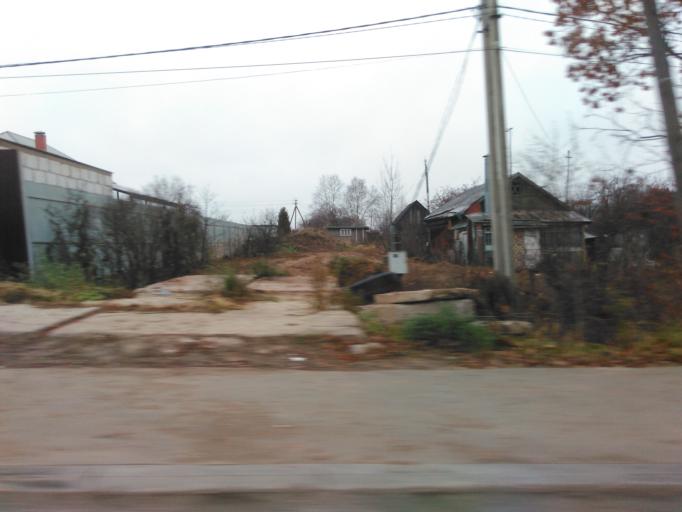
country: RU
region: Moskovskaya
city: Sofrino
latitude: 56.1203
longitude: 37.9658
